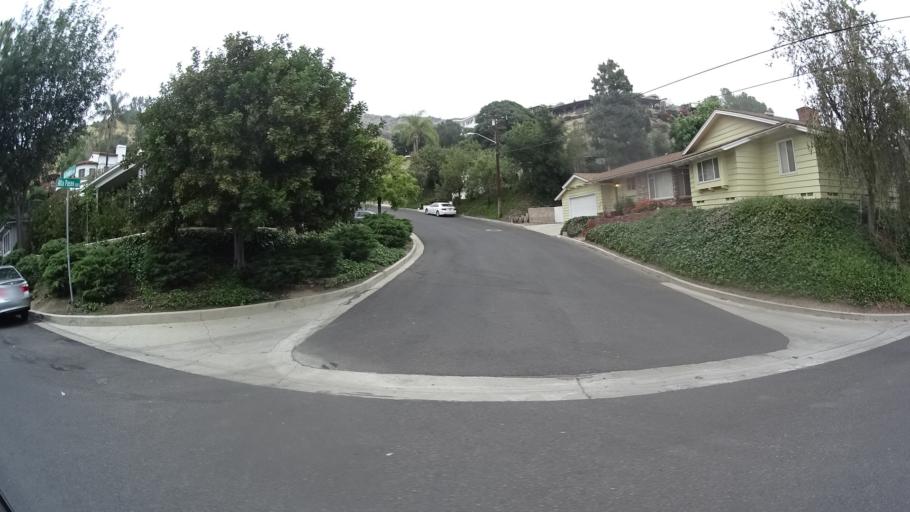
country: US
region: California
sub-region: Los Angeles County
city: Burbank
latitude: 34.1903
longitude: -118.2911
